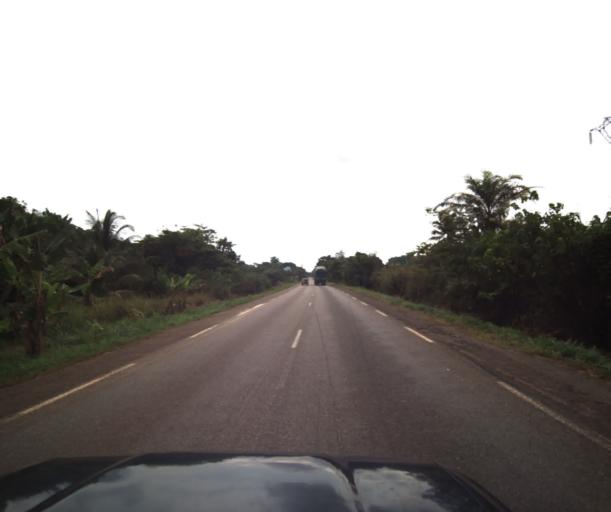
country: CM
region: Littoral
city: Edea
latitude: 3.8352
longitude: 10.4333
